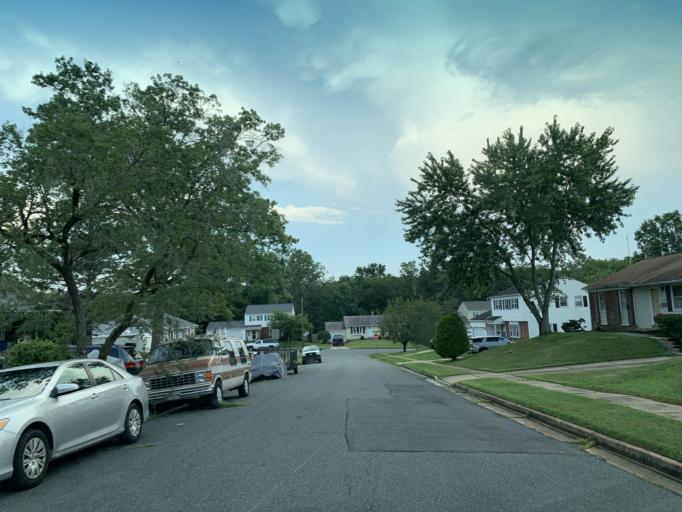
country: US
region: Maryland
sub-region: Harford County
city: Joppatowne
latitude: 39.4083
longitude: -76.3453
